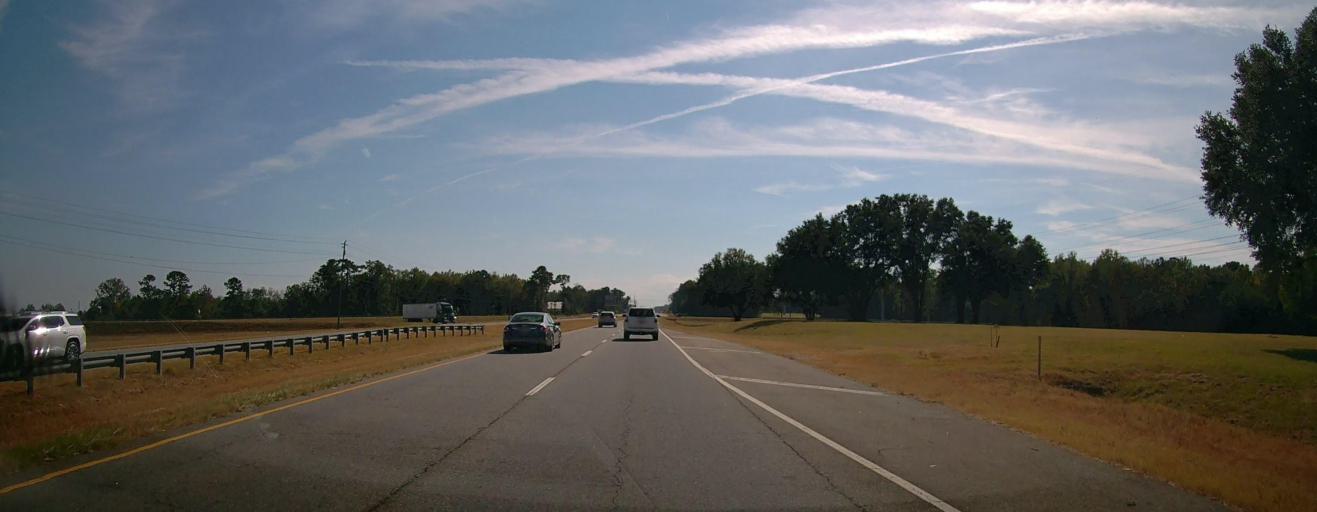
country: US
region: Georgia
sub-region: Dougherty County
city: Albany
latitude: 31.5457
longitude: -84.1151
